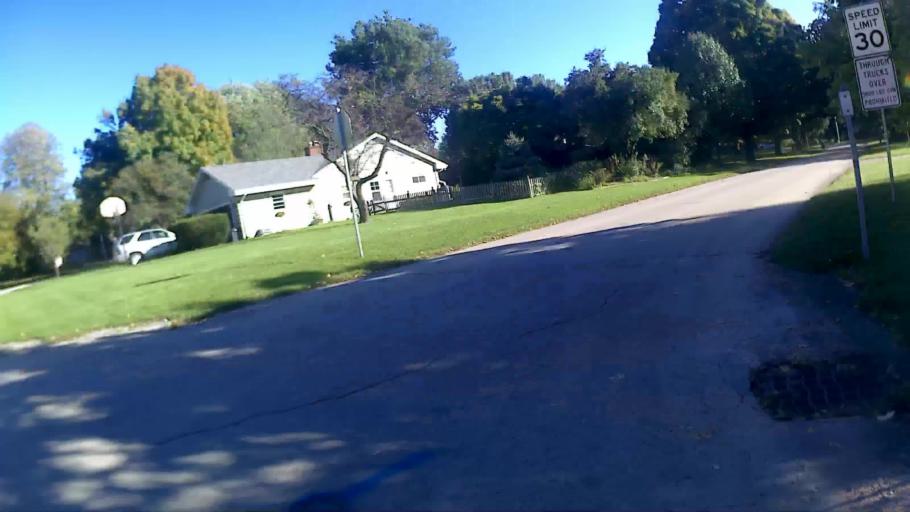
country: US
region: Illinois
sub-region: DuPage County
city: Wheaton
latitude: 41.8576
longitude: -88.1049
